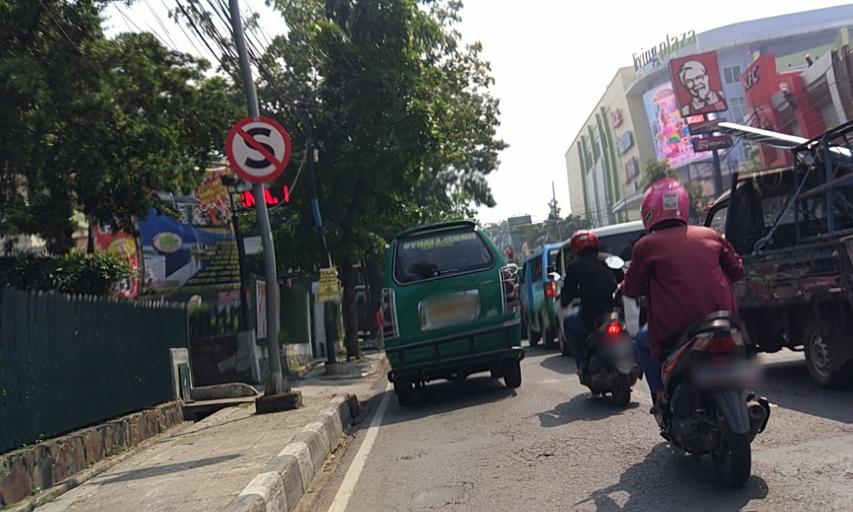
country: ID
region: West Java
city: Bandung
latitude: -6.9074
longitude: 107.5976
